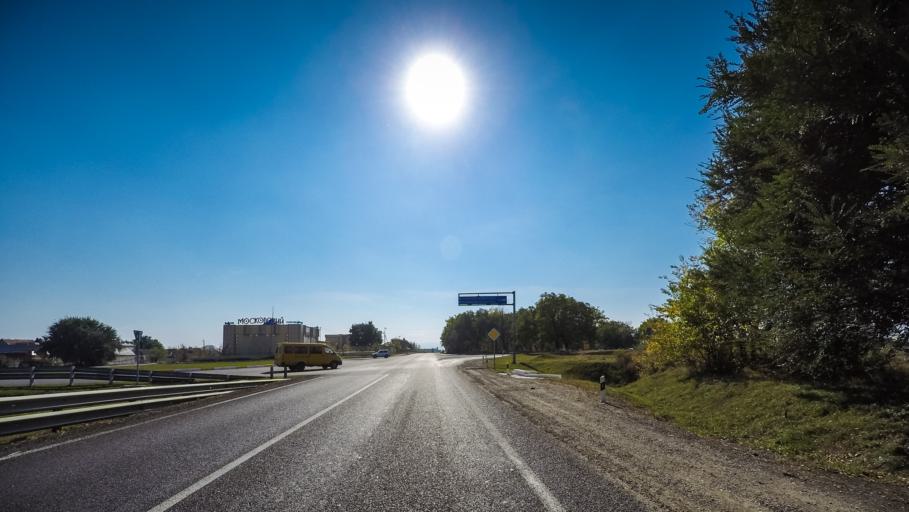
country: RU
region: Kabardino-Balkariya
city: Chegem Vtoroy
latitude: 43.5813
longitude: 43.5807
